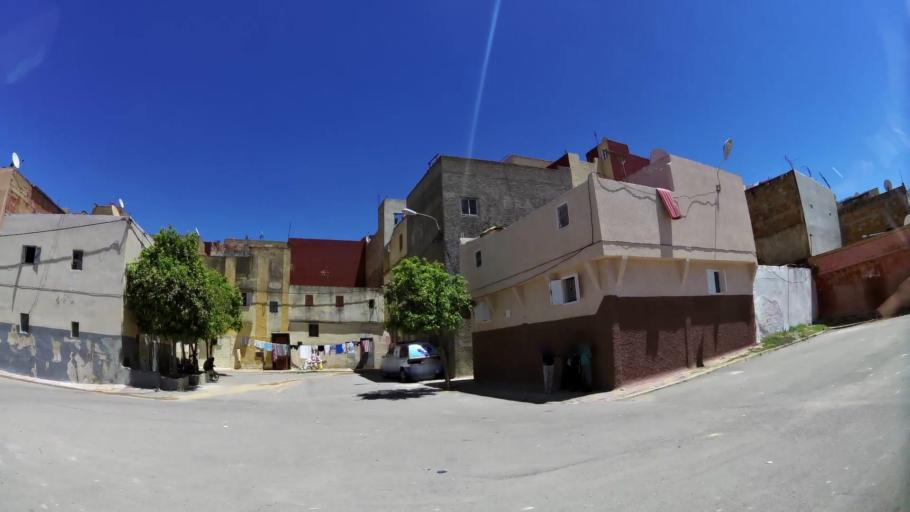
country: MA
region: Meknes-Tafilalet
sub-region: Meknes
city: Meknes
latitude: 33.9137
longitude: -5.5806
